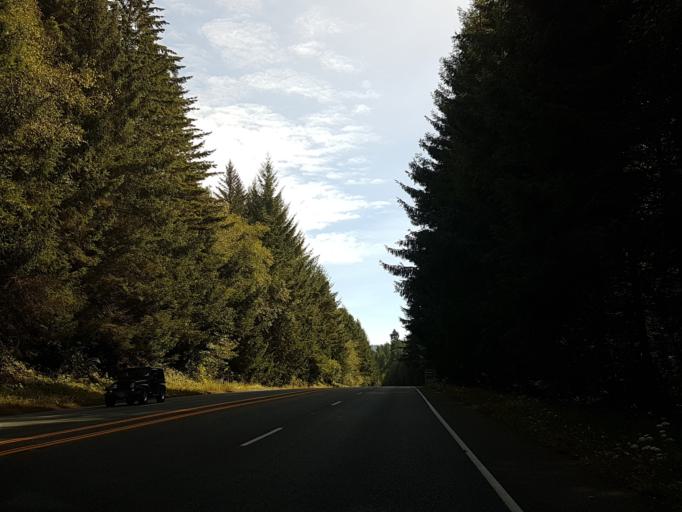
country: US
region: California
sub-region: Del Norte County
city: Bertsch-Oceanview
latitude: 41.4814
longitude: -124.0495
